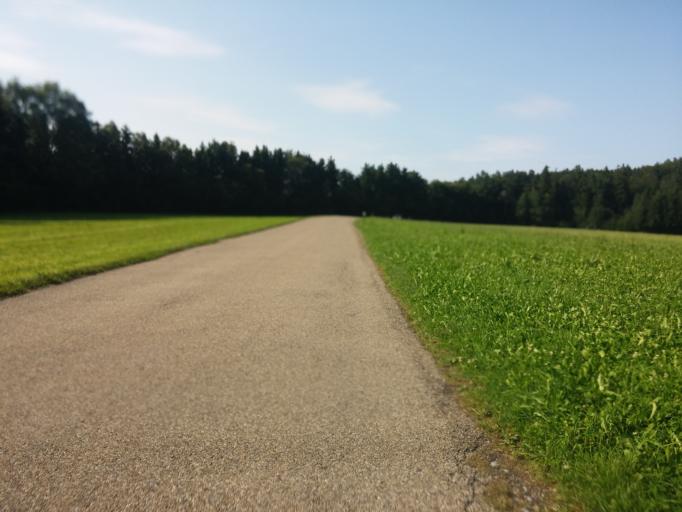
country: DE
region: Baden-Wuerttemberg
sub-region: Tuebingen Region
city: Aitrach
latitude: 47.9302
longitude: 10.1148
